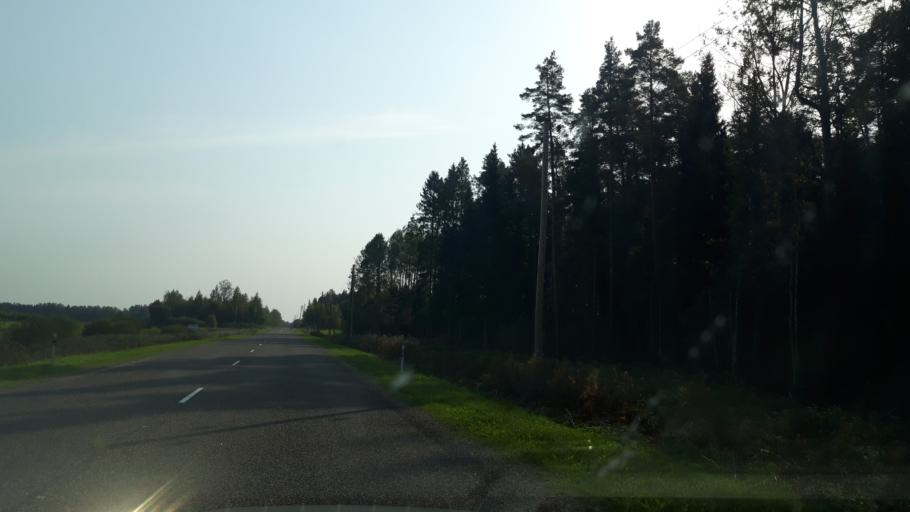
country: LV
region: Burtnieki
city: Matisi
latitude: 57.6408
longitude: 25.2494
